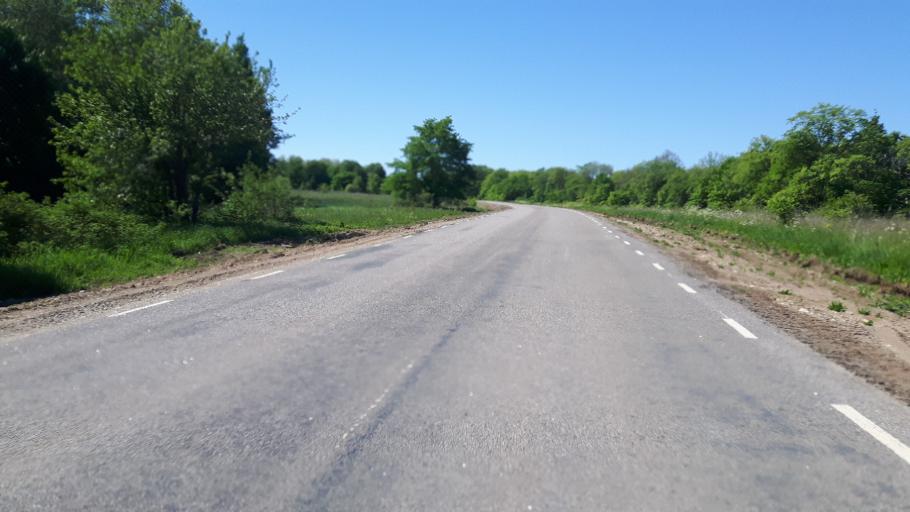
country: EE
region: Ida-Virumaa
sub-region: Narva-Joesuu linn
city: Narva-Joesuu
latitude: 59.4108
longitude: 27.9487
